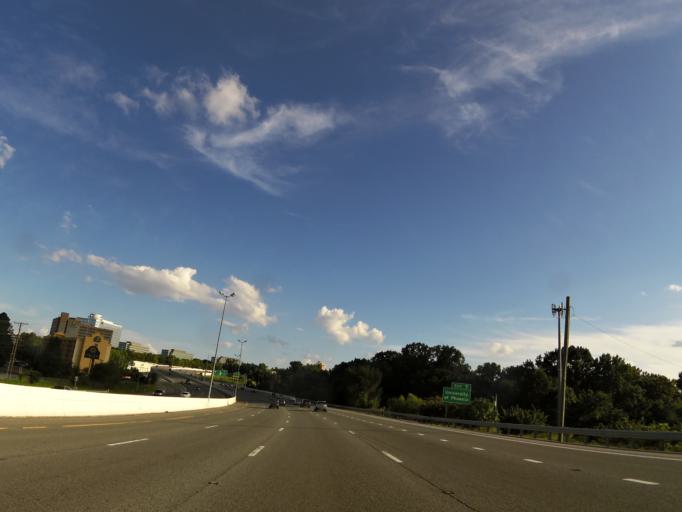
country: US
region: Tennessee
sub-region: Davidson County
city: Nashville
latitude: 36.1578
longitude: -86.6927
